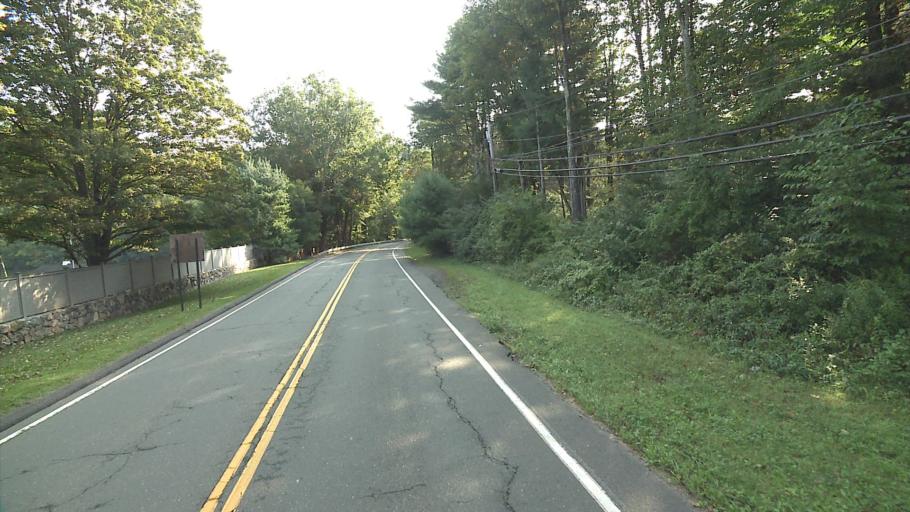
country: US
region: Connecticut
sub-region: Fairfield County
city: Newtown
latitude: 41.4369
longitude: -73.2688
